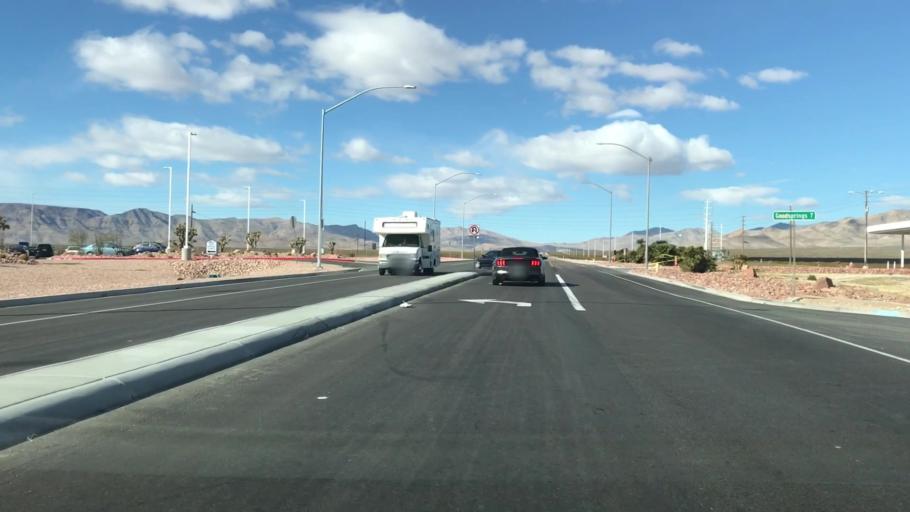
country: US
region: Nevada
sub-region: Clark County
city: Enterprise
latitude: 35.7823
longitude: -115.3315
